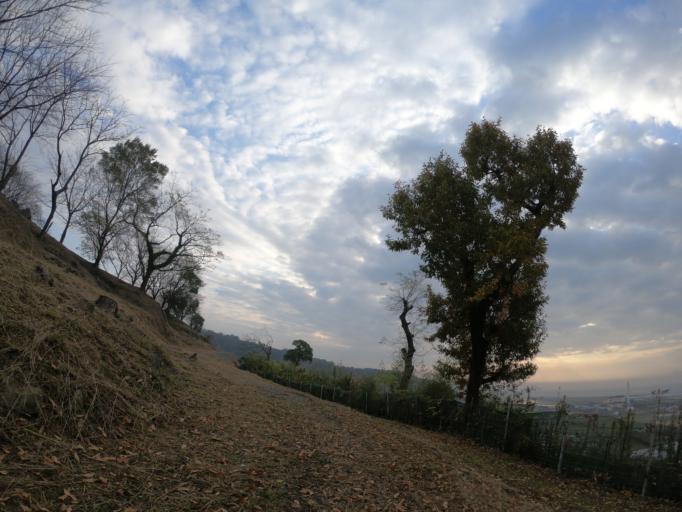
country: JP
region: Nagasaki
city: Shimabara
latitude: 32.6590
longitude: 130.2528
